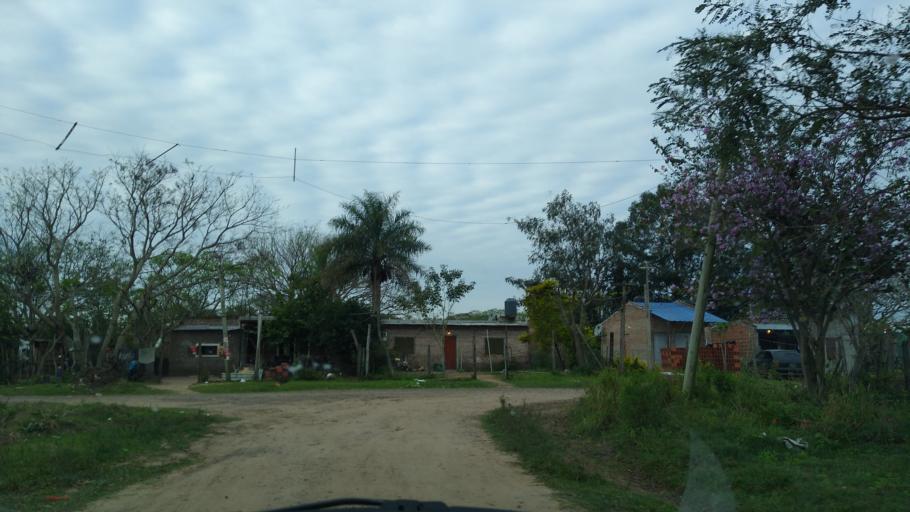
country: AR
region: Chaco
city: Fontana
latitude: -27.4015
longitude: -59.0376
